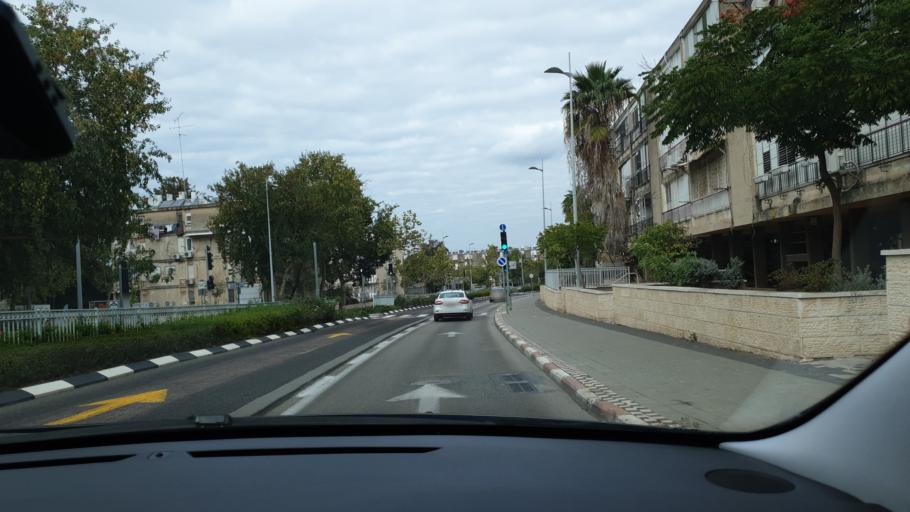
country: IL
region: Haifa
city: Qiryat Ata
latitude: 32.8145
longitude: 35.1138
